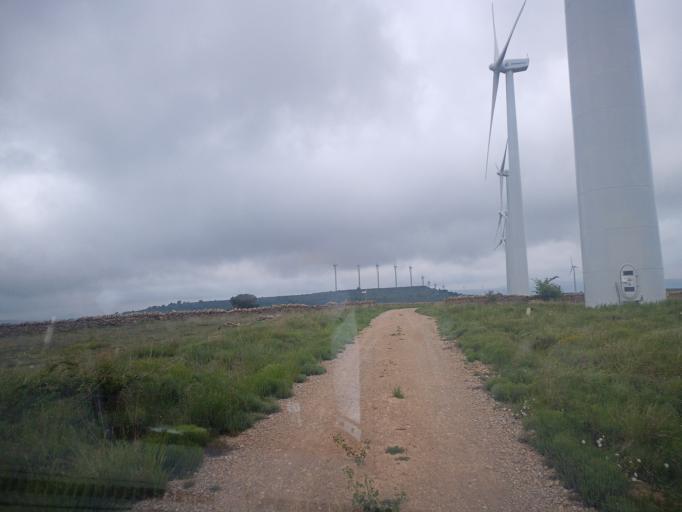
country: ES
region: Valencia
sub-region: Provincia de Castello
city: Castellfort
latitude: 40.4657
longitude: -0.1961
